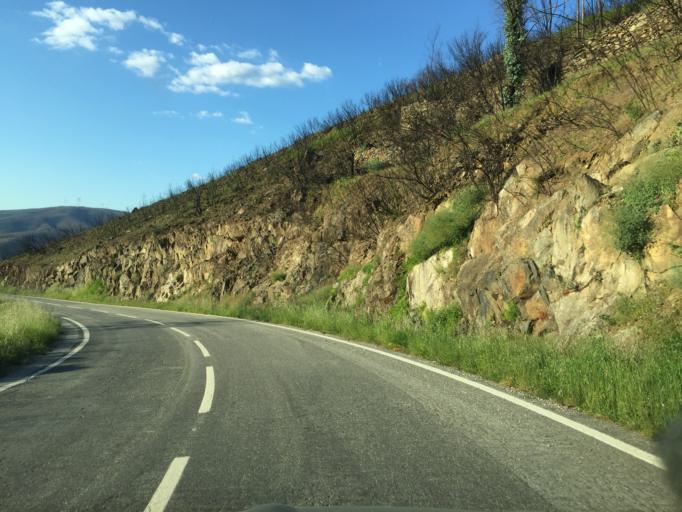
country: PT
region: Coimbra
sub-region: Pampilhosa da Serra
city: Pampilhosa da Serra
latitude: 40.0325
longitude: -7.9599
